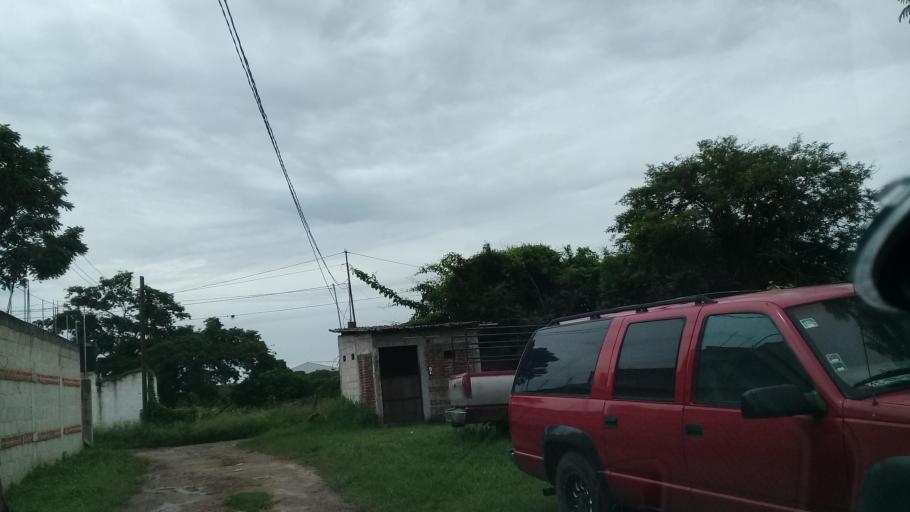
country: MX
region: Veracruz
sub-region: Emiliano Zapata
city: Dos Rios
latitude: 19.4789
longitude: -96.7986
